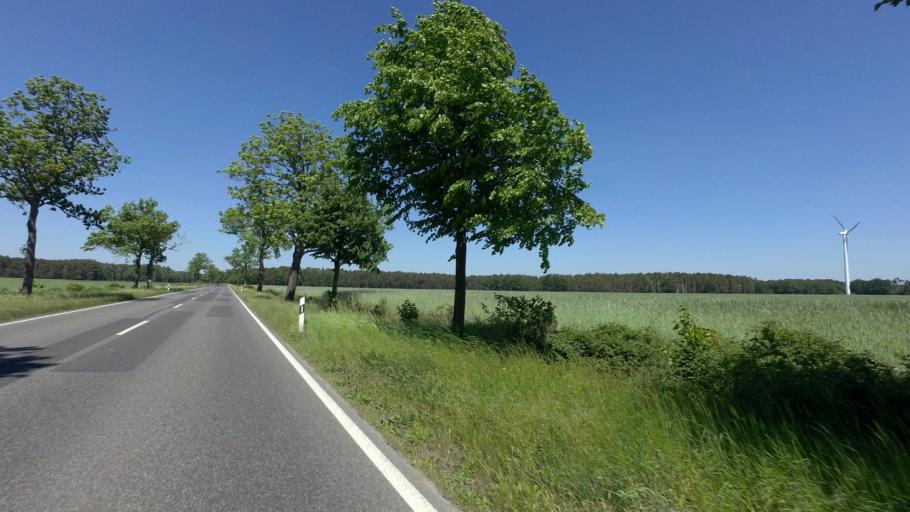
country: DE
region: Brandenburg
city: Drehnow
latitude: 51.8833
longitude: 14.3732
